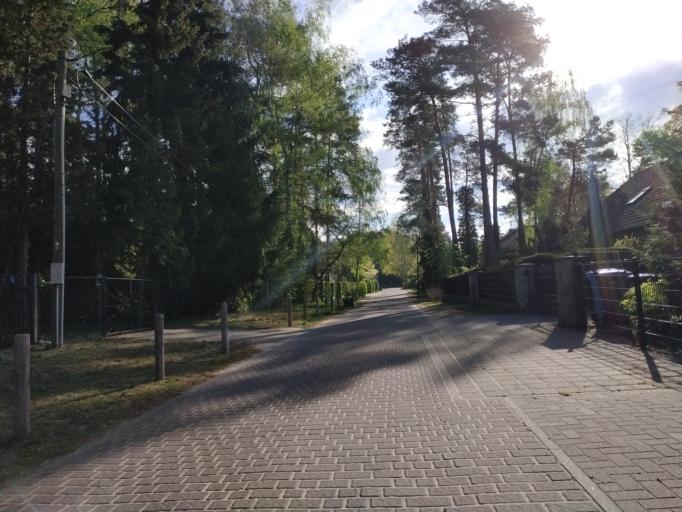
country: DE
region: Brandenburg
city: Petershagen
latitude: 52.5463
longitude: 13.8314
